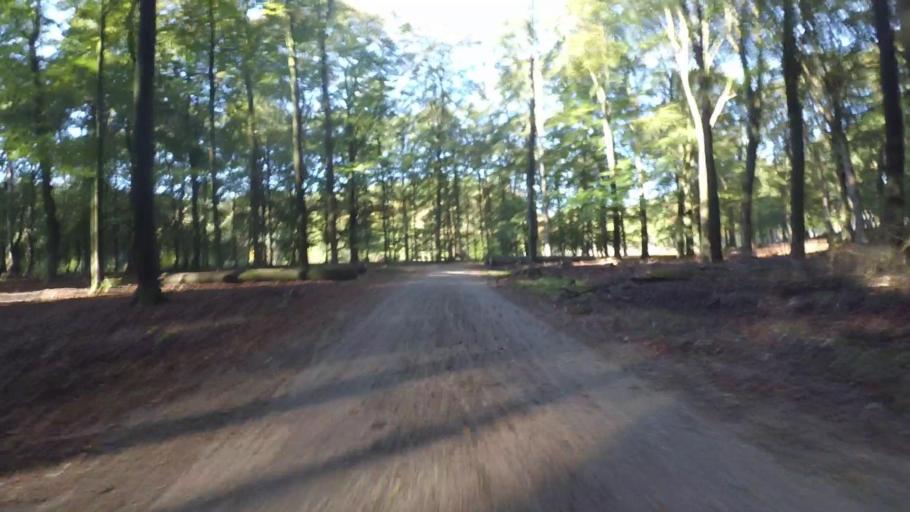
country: NL
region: Gelderland
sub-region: Gemeente Apeldoorn
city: Apeldoorn
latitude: 52.2314
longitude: 5.8795
